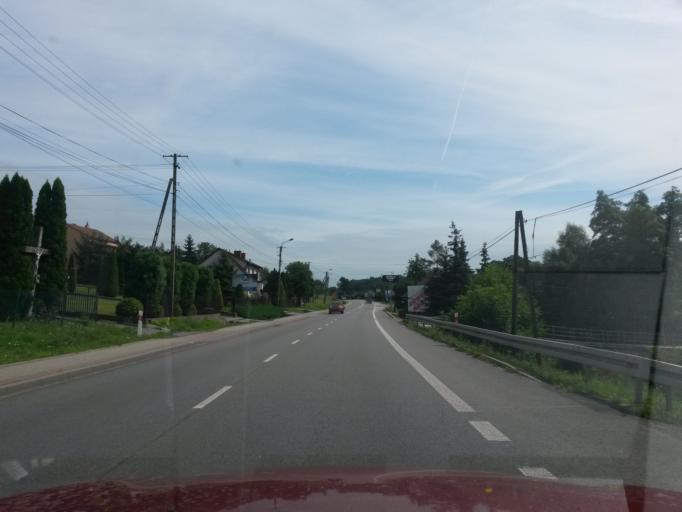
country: PL
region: Lesser Poland Voivodeship
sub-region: Powiat bochenski
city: Lapczyca
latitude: 49.9599
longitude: 20.3822
